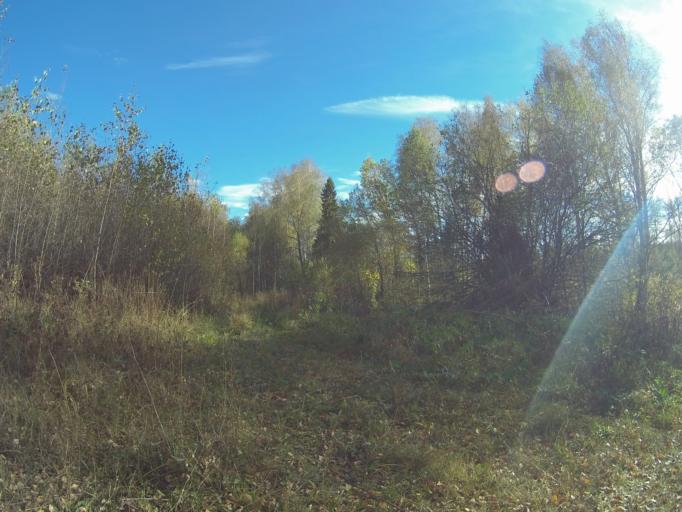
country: RU
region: Vladimir
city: Golovino
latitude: 56.0015
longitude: 40.4989
